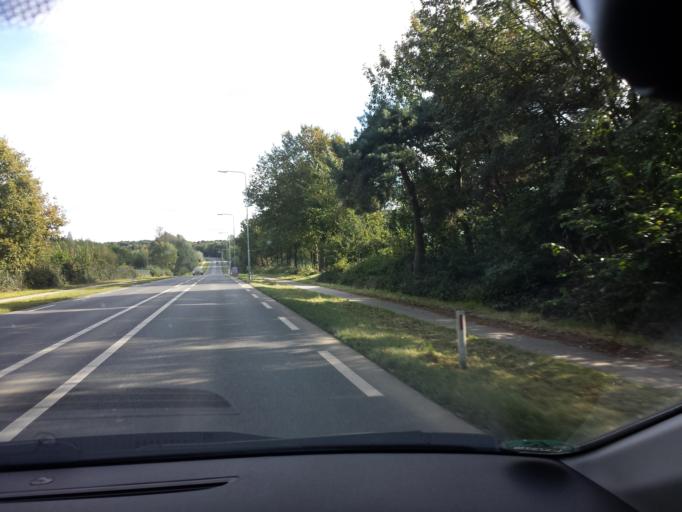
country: NL
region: Limburg
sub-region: Gemeente Brunssum
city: Brunssum
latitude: 50.9320
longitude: 6.0211
